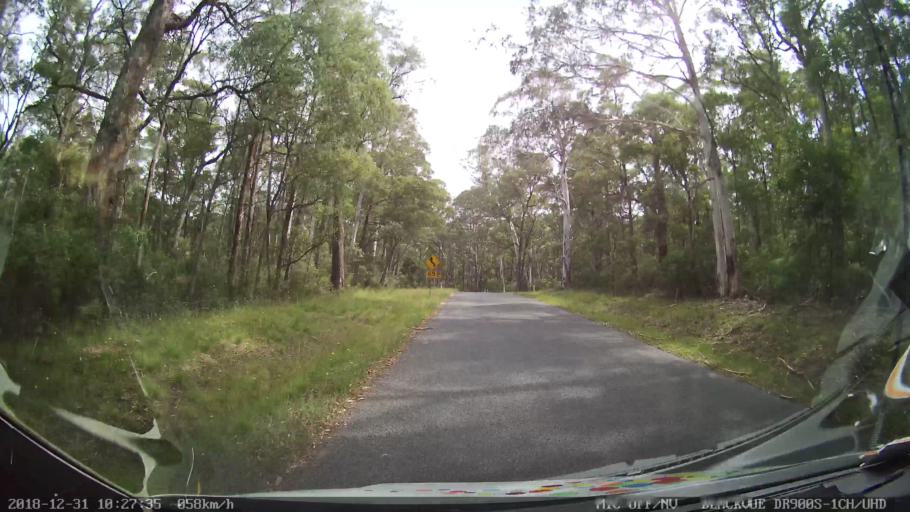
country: AU
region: New South Wales
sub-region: Snowy River
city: Jindabyne
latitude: -36.4855
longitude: 148.1448
